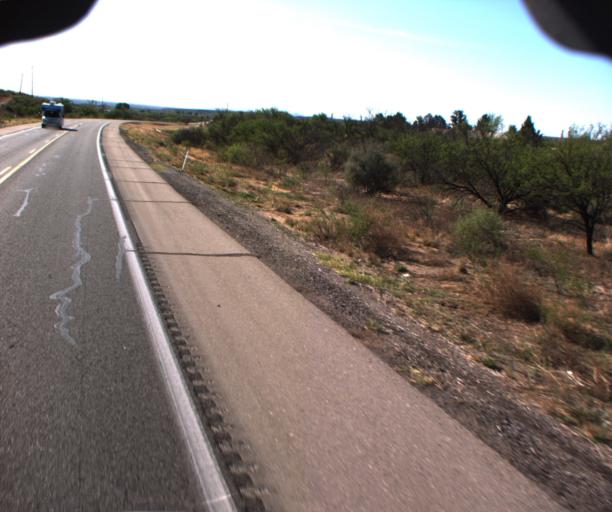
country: US
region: Arizona
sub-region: Cochise County
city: Saint David
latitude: 31.9200
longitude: -110.2669
